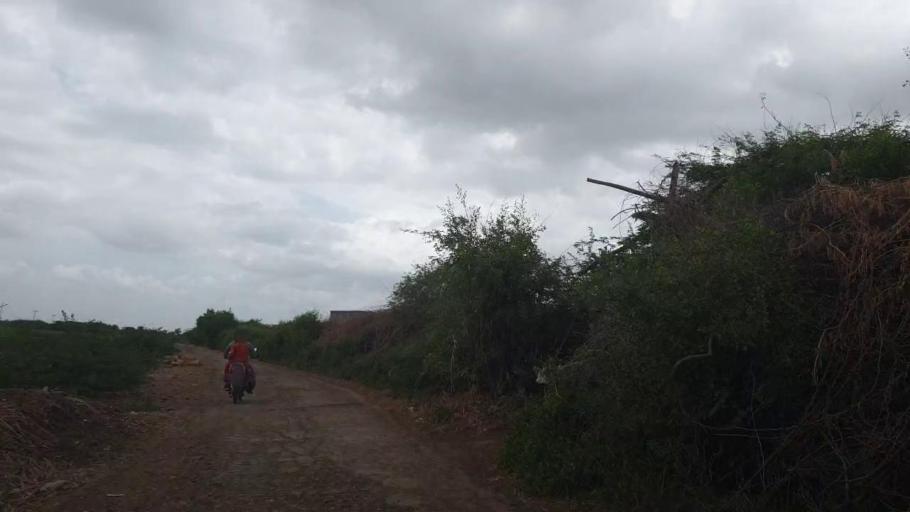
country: PK
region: Sindh
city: Badin
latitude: 24.6549
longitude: 68.9464
